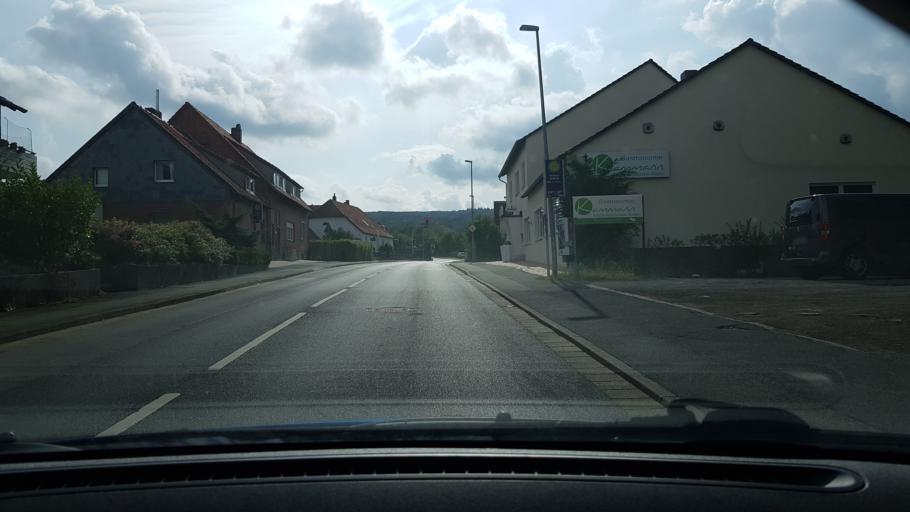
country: DE
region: Lower Saxony
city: Egestorf
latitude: 52.2923
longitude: 9.4894
